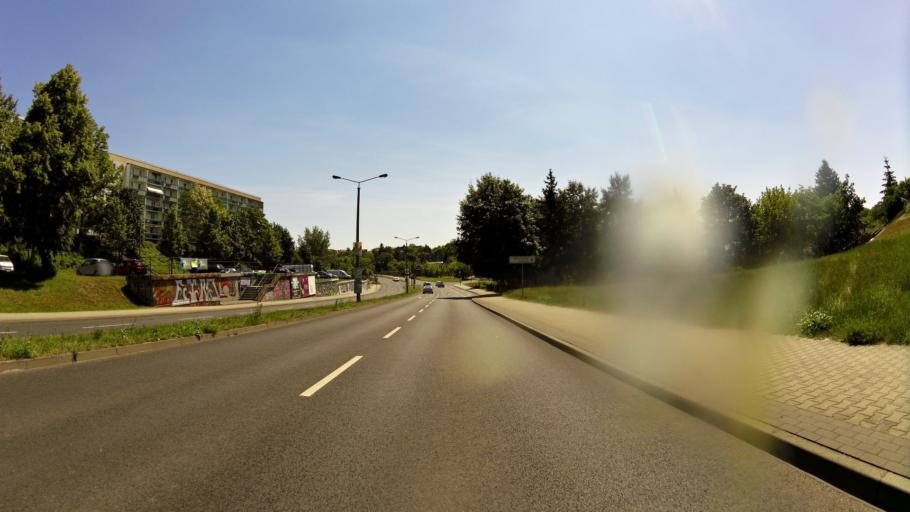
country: DE
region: Brandenburg
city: Frankfurt (Oder)
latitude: 52.3534
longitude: 14.5311
